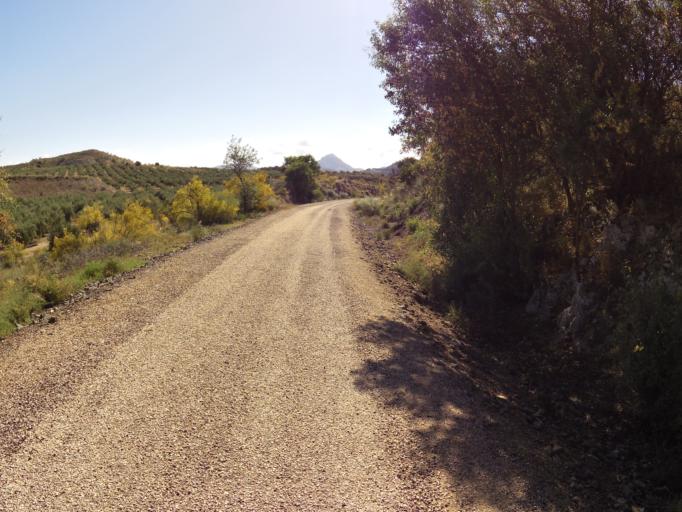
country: ES
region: Andalusia
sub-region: Provincia de Jaen
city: Alcaudete
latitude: 37.6054
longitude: -4.1555
